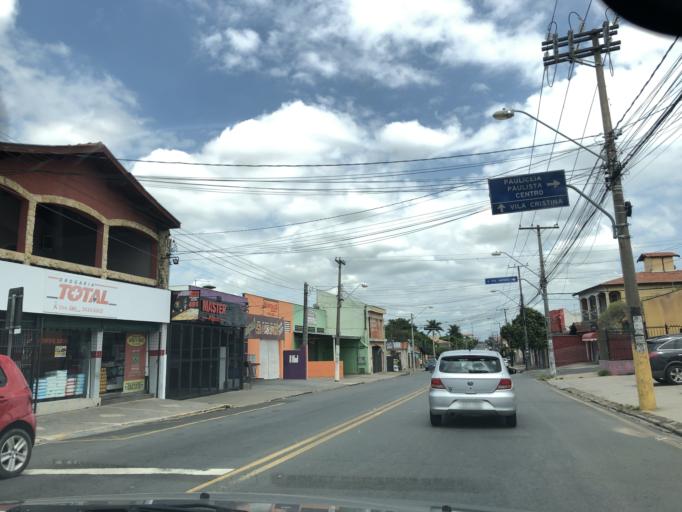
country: BR
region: Sao Paulo
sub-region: Piracicaba
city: Piracicaba
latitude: -22.7504
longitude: -47.6534
